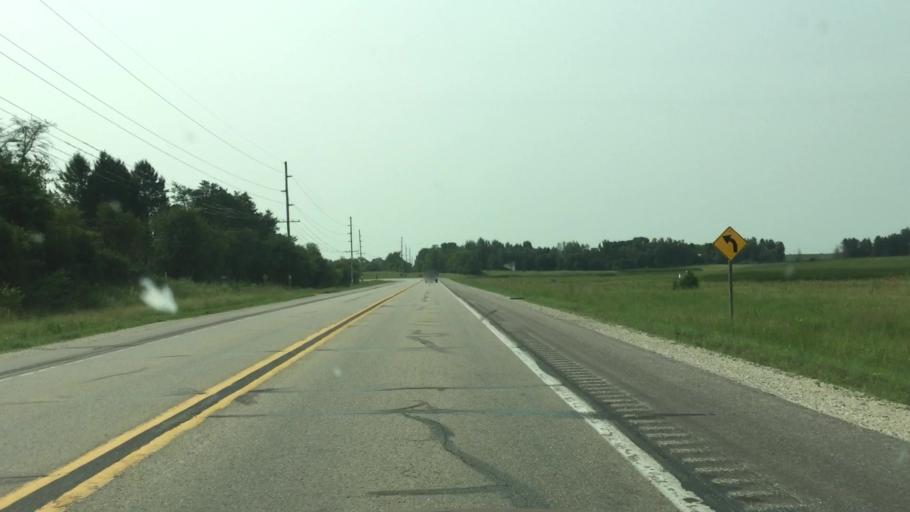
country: US
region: Iowa
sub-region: Dickinson County
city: Milford
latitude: 43.3488
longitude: -95.1798
